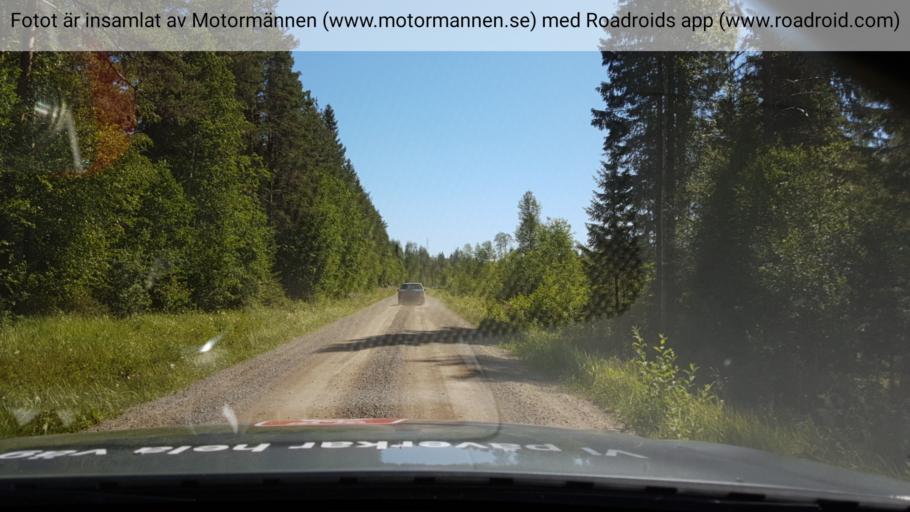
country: SE
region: Jaemtland
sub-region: Braecke Kommun
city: Braecke
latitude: 62.7975
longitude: 15.2580
